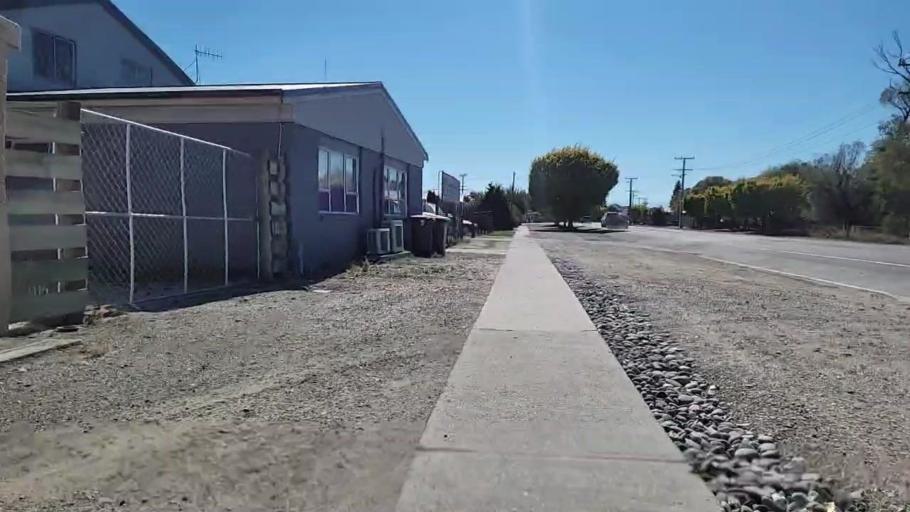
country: NZ
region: Otago
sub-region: Queenstown-Lakes District
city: Wanaka
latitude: -45.0975
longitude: 169.5983
